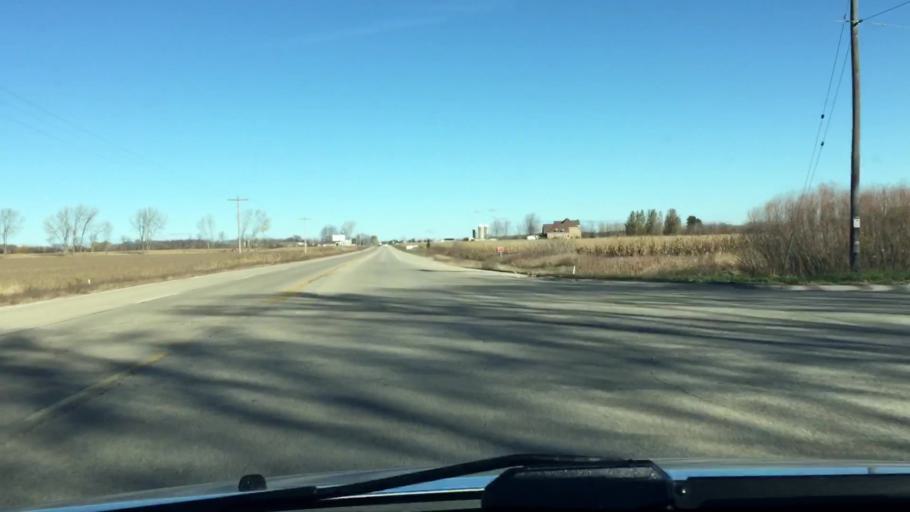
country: US
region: Wisconsin
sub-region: Brown County
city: Pulaski
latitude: 44.6143
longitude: -88.2205
